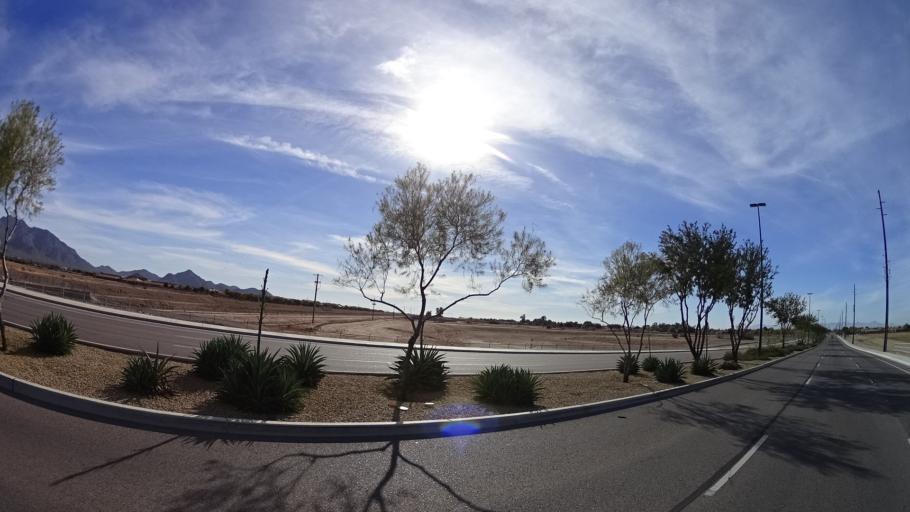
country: US
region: Arizona
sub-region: Maricopa County
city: Queen Creek
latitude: 33.2194
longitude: -111.7414
